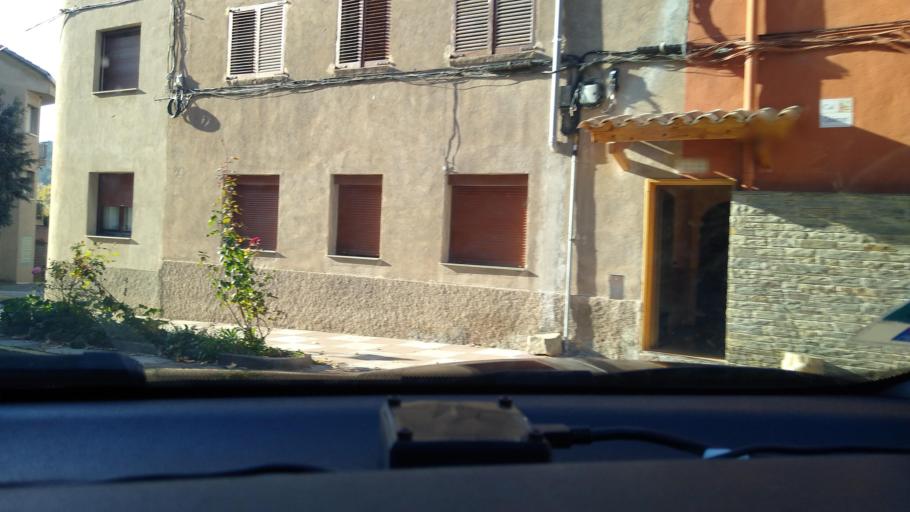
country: ES
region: Catalonia
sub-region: Provincia de Barcelona
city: Baga
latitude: 42.2509
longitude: 1.8644
